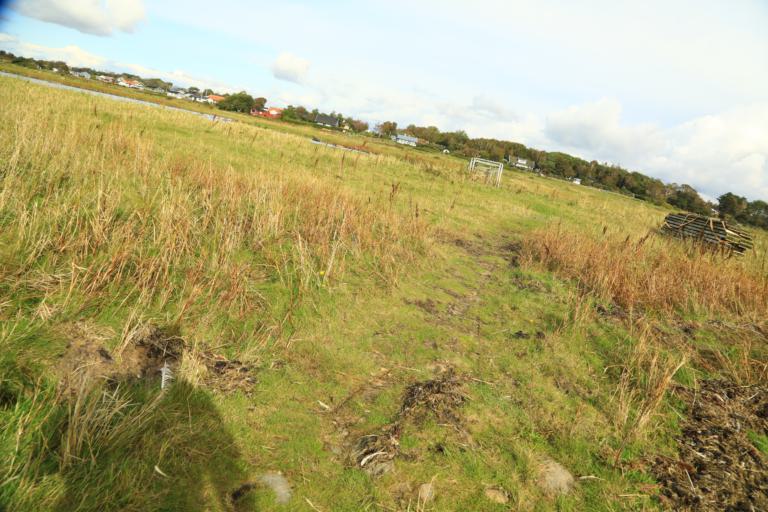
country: SE
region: Halland
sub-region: Varbergs Kommun
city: Traslovslage
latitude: 57.0194
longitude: 12.3342
